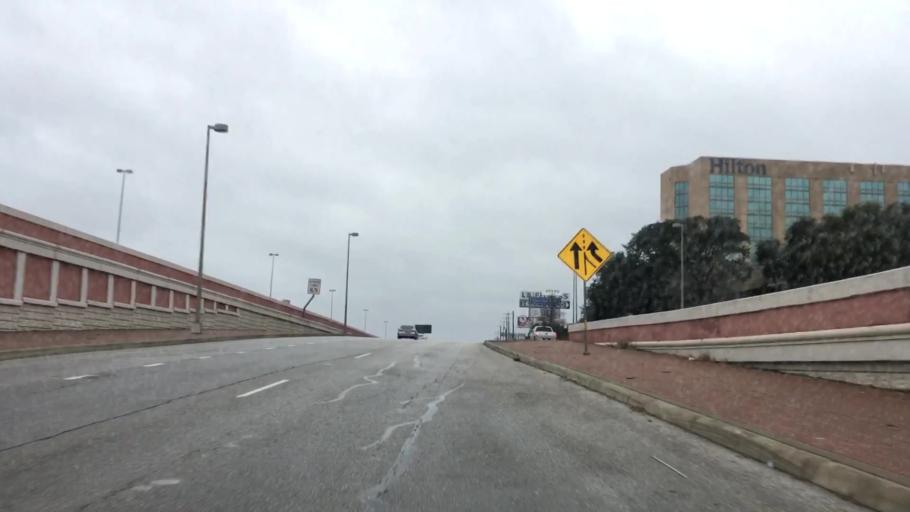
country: US
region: Texas
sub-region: Bexar County
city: Castle Hills
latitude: 29.5209
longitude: -98.5005
